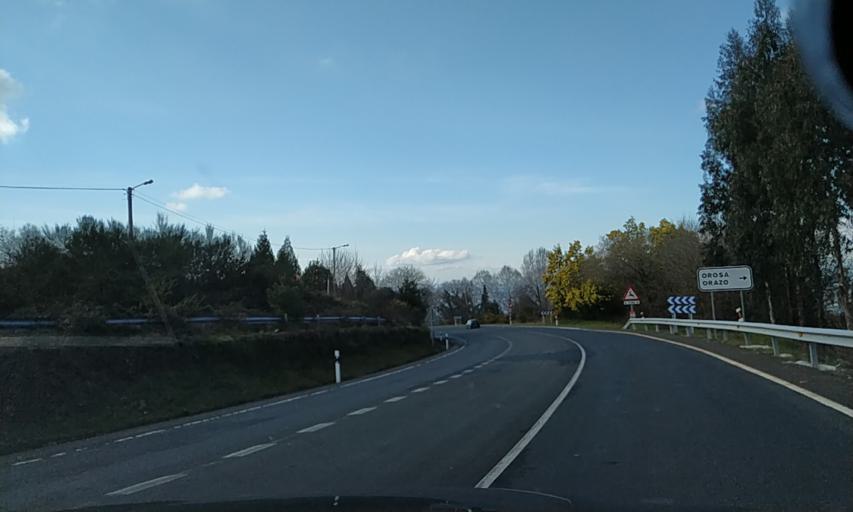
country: ES
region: Galicia
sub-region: Provincia da Coruna
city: Ribeira
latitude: 42.7140
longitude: -8.3728
